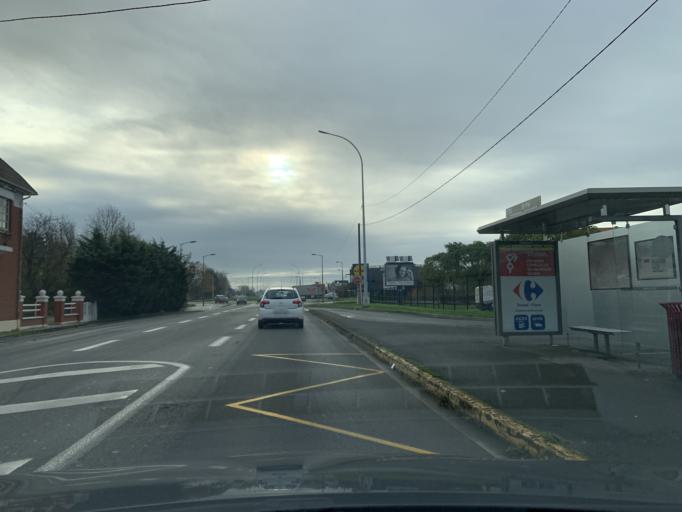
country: FR
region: Nord-Pas-de-Calais
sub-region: Departement du Nord
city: Dechy
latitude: 50.3451
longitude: 3.0920
